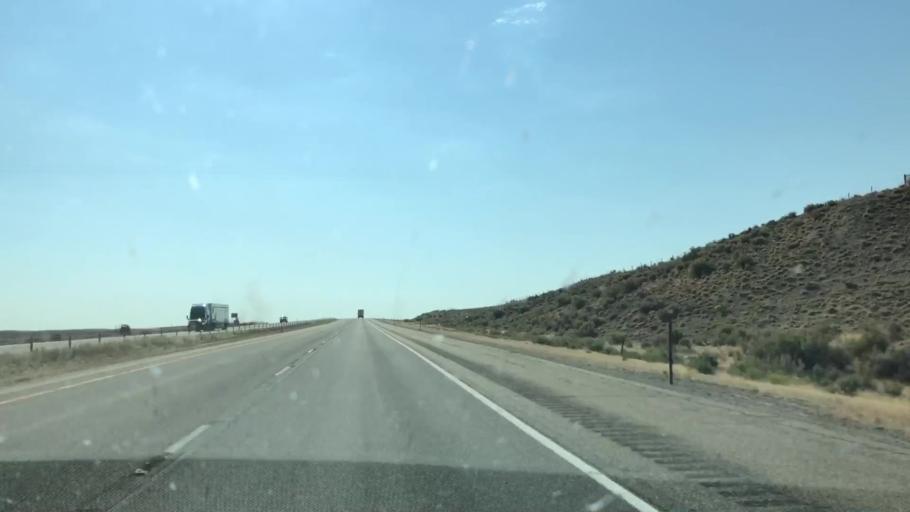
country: US
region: Wyoming
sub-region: Sweetwater County
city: Rock Springs
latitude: 41.6601
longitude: -108.7182
